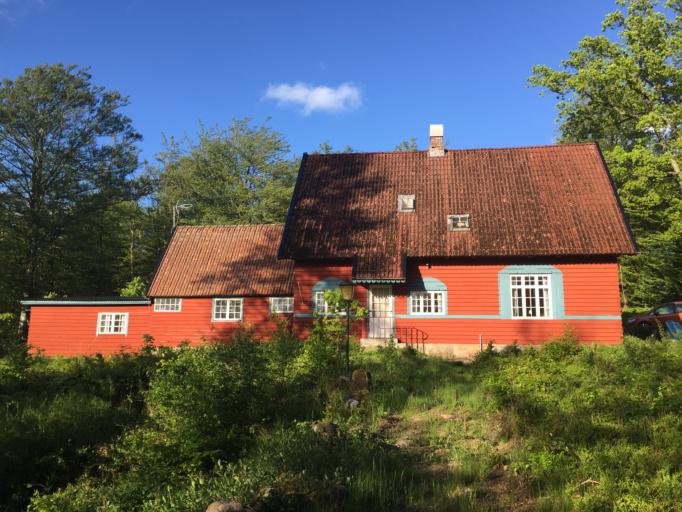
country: SE
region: Kronoberg
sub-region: Markaryds Kommun
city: Markaryd
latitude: 56.5176
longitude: 13.6060
